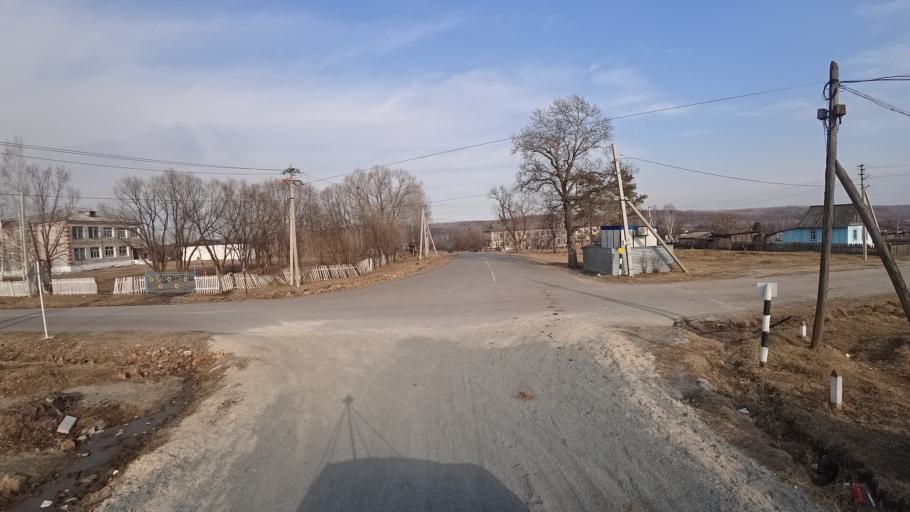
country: RU
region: Amur
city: Novobureyskiy
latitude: 49.8965
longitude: 129.8772
